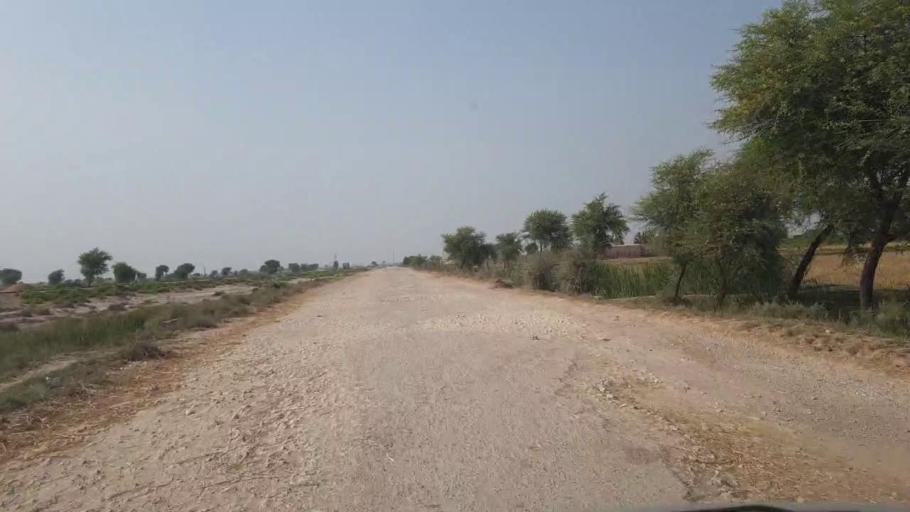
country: PK
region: Sindh
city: Matli
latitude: 25.0238
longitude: 68.6784
